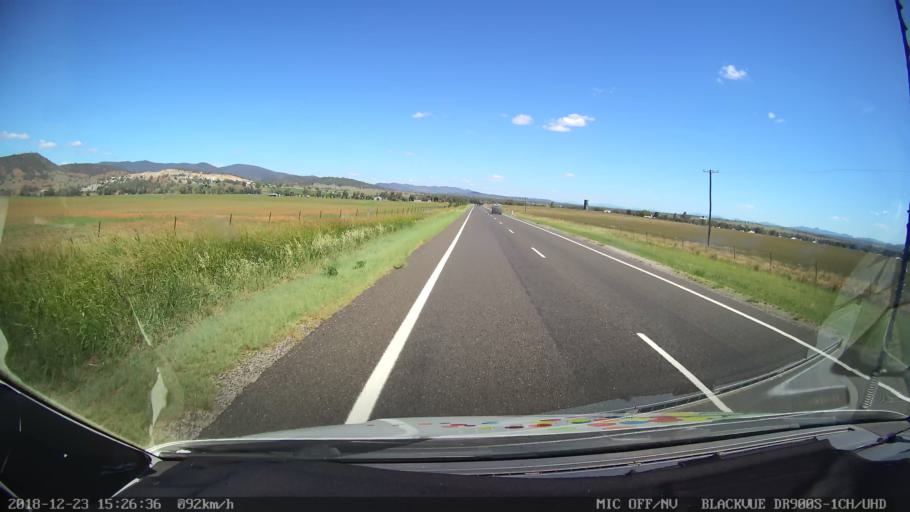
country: AU
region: New South Wales
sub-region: Tamworth Municipality
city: East Tamworth
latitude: -30.9187
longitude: 150.8395
